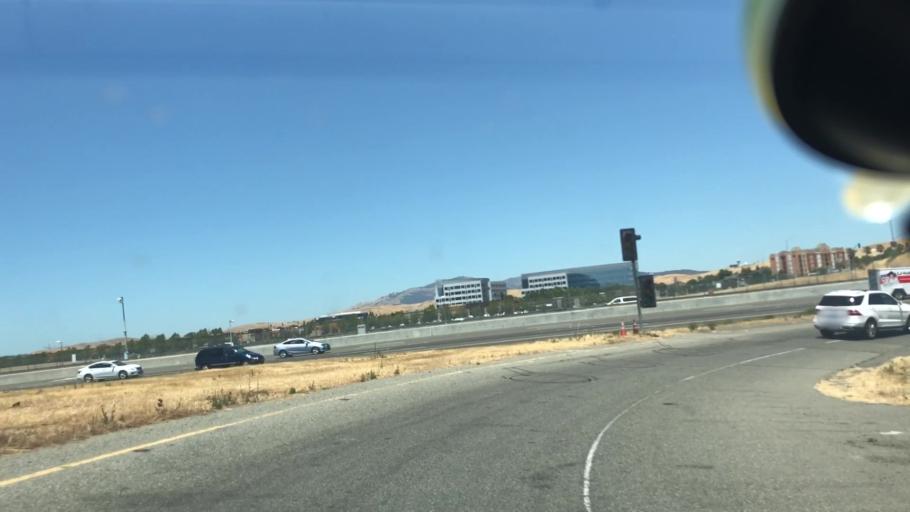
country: US
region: California
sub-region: Alameda County
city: Pleasanton
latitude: 37.7009
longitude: -121.8893
